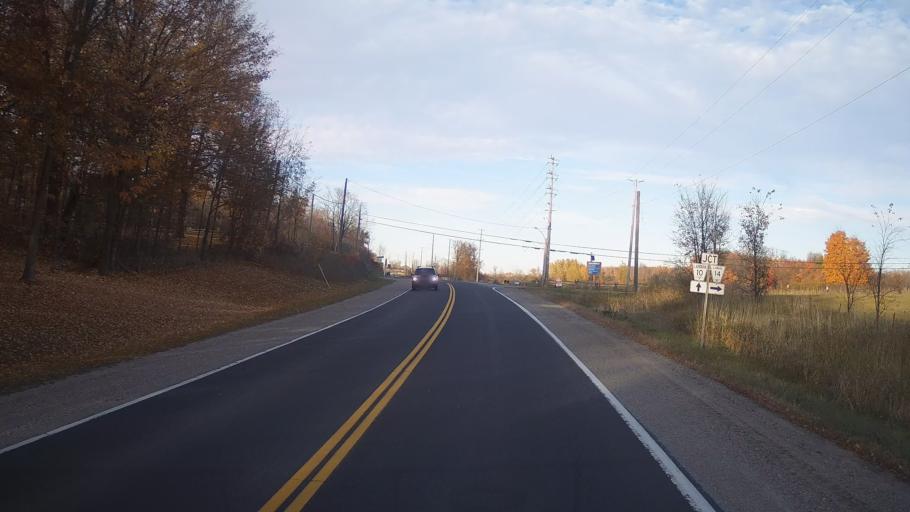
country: CA
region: Ontario
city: Perth
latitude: 44.8267
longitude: -76.3153
